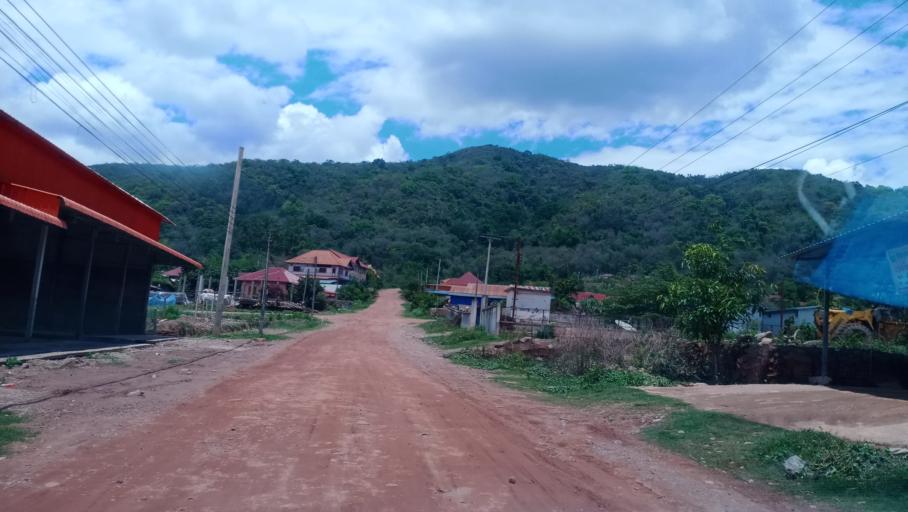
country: CN
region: Yunnan
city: Menglie
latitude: 22.1265
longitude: 101.7905
